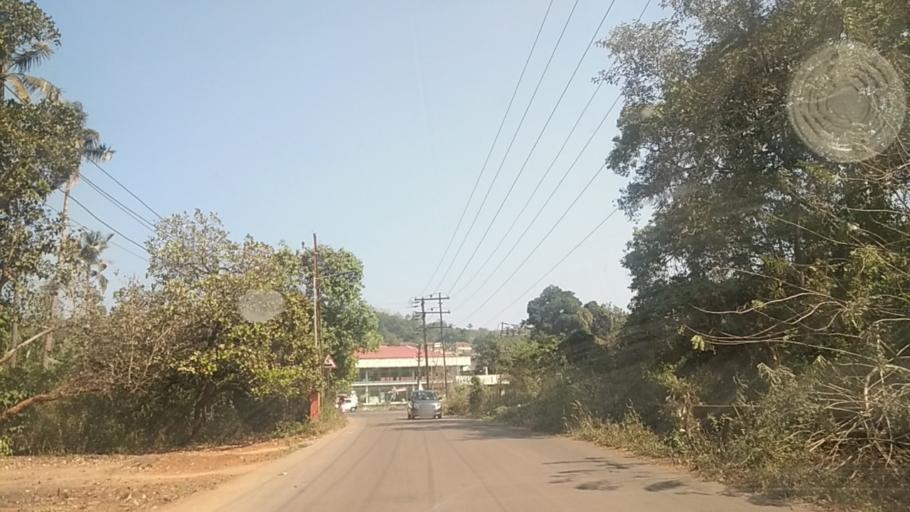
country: IN
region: Goa
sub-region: South Goa
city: Raia
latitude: 15.3246
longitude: 73.9365
